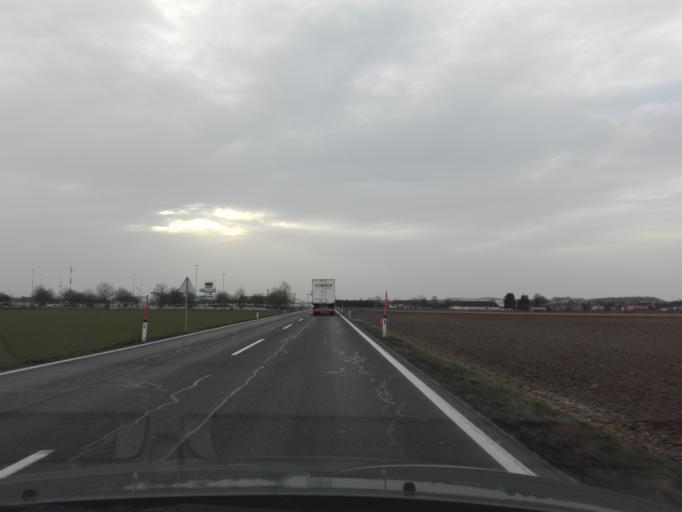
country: AT
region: Upper Austria
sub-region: Politischer Bezirk Linz-Land
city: Pasching
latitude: 48.2422
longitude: 14.2010
